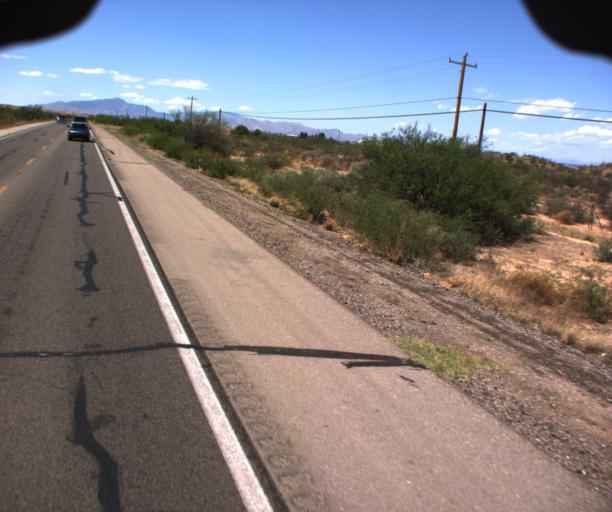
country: US
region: Arizona
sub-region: Cochise County
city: Benson
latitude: 31.9204
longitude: -110.2674
